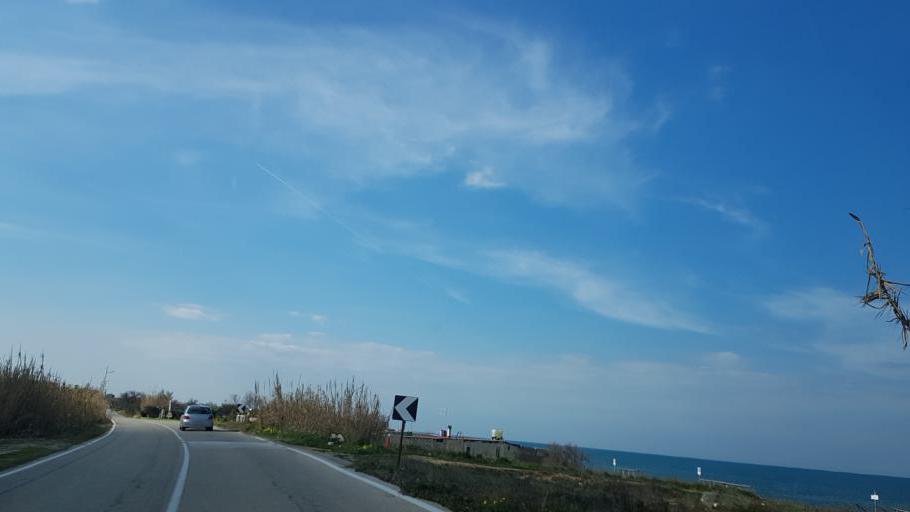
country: IT
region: Apulia
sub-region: Provincia di Brindisi
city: Brindisi
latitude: 40.6840
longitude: 17.8816
